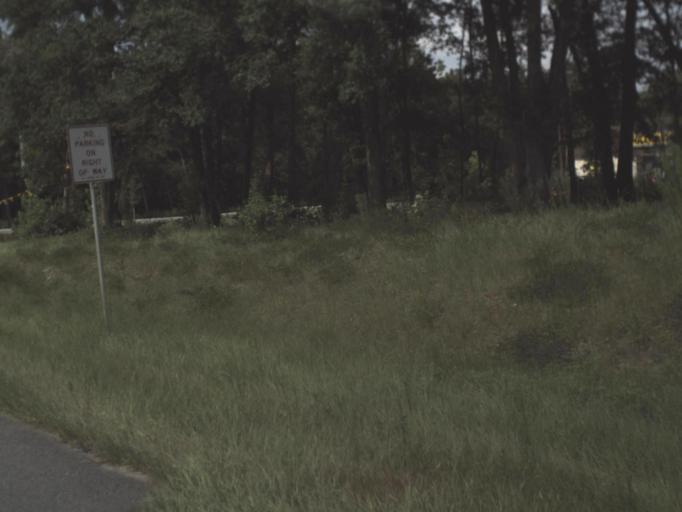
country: US
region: Florida
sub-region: Citrus County
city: Pine Ridge
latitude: 28.9637
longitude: -82.4186
